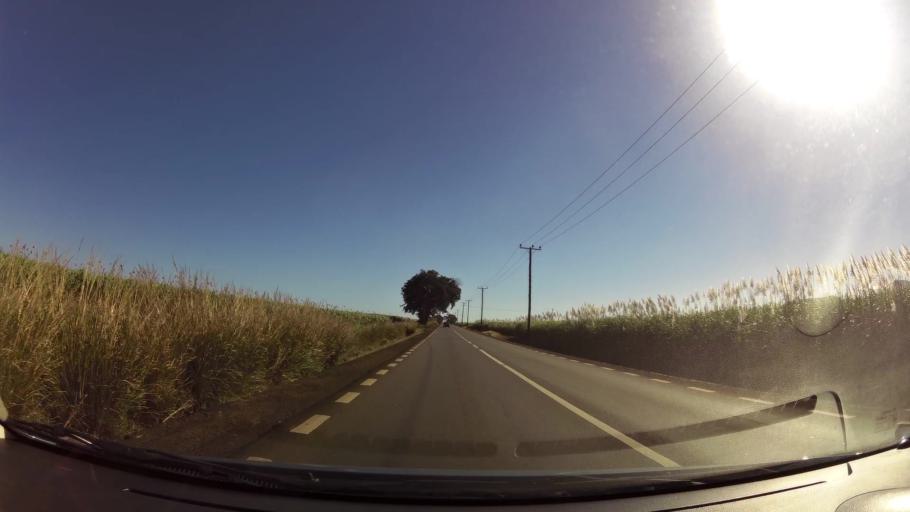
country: MU
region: Black River
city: Cascavelle
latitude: -20.3082
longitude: 57.4022
